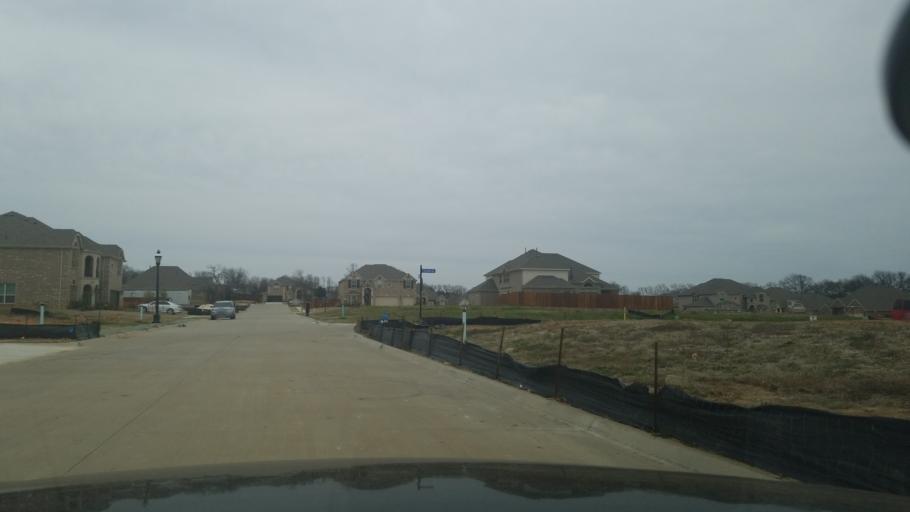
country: US
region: Texas
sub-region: Denton County
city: Corinth
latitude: 33.1332
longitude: -97.0783
